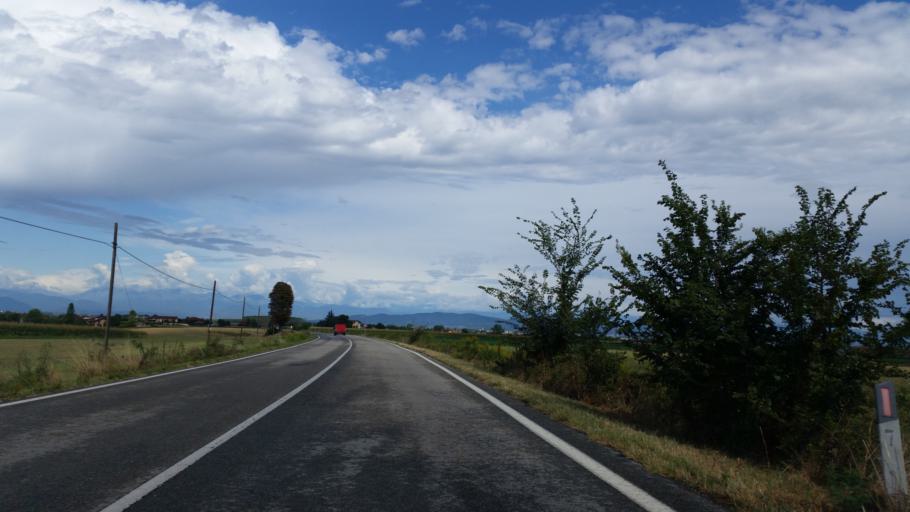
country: IT
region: Piedmont
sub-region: Provincia di Torino
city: Pralormo
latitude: 44.8804
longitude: 7.8812
